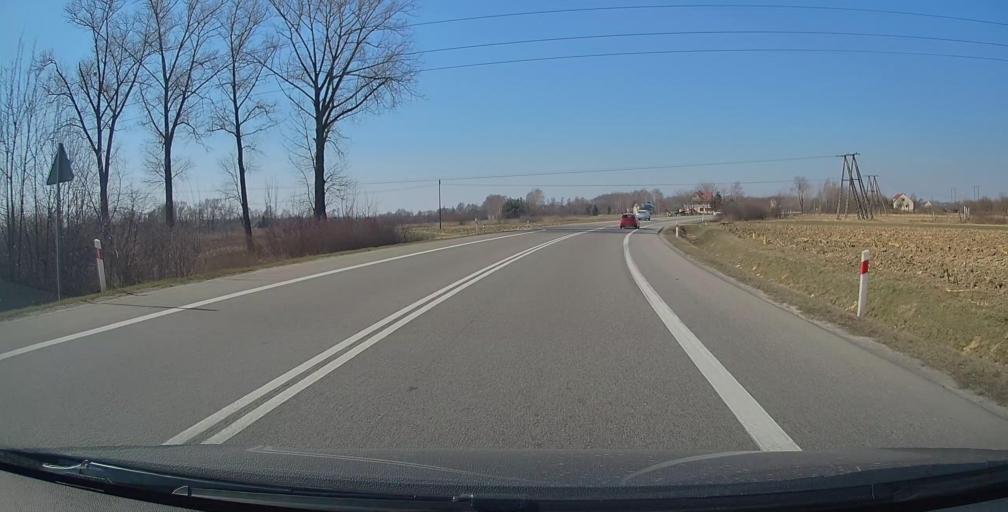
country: PL
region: Subcarpathian Voivodeship
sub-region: Powiat nizanski
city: Zarzecze
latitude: 50.5162
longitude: 22.1848
